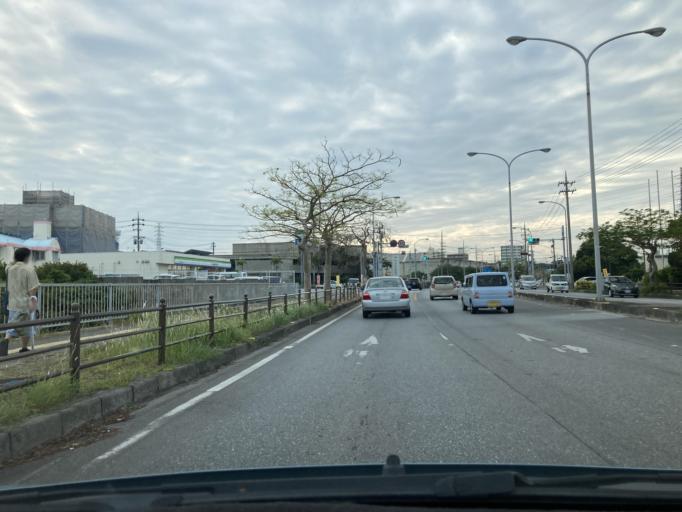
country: JP
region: Okinawa
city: Okinawa
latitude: 26.3531
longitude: 127.8100
